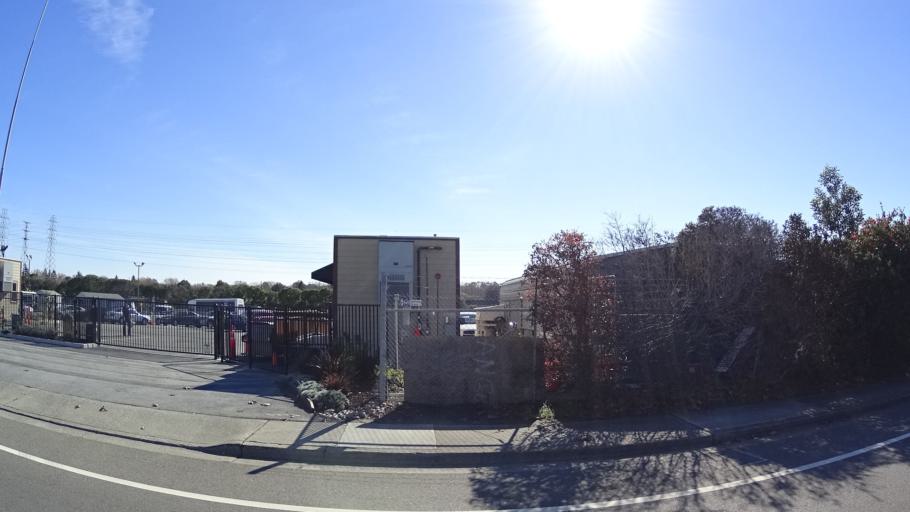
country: US
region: California
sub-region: San Mateo County
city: Burlingame
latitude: 37.5894
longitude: -122.3445
